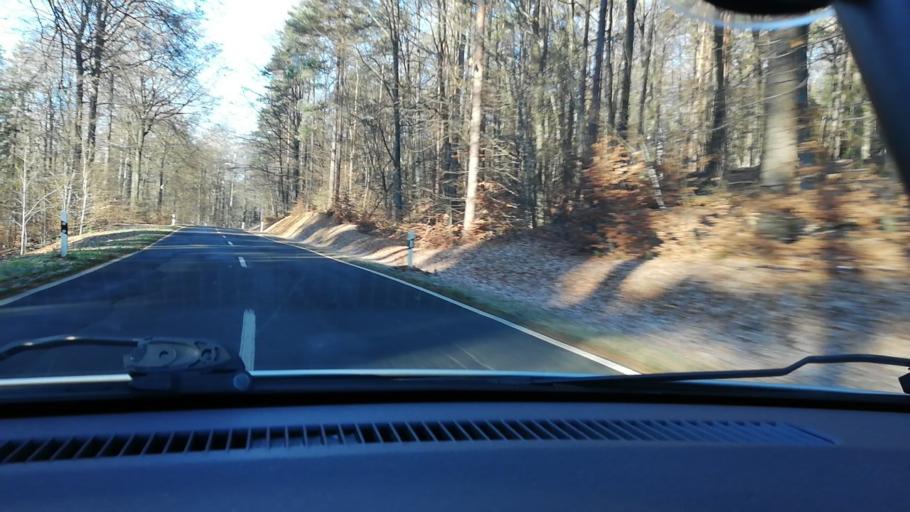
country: DE
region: Bavaria
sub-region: Regierungsbezirk Unterfranken
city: Heigenbrucken
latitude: 49.9983
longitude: 9.3716
